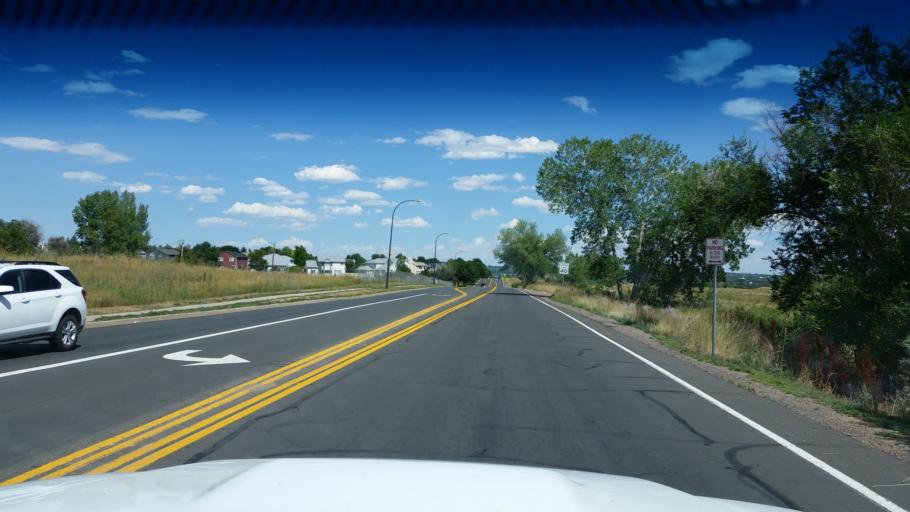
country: US
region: Colorado
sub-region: Broomfield County
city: Broomfield
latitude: 39.8782
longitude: -105.1281
